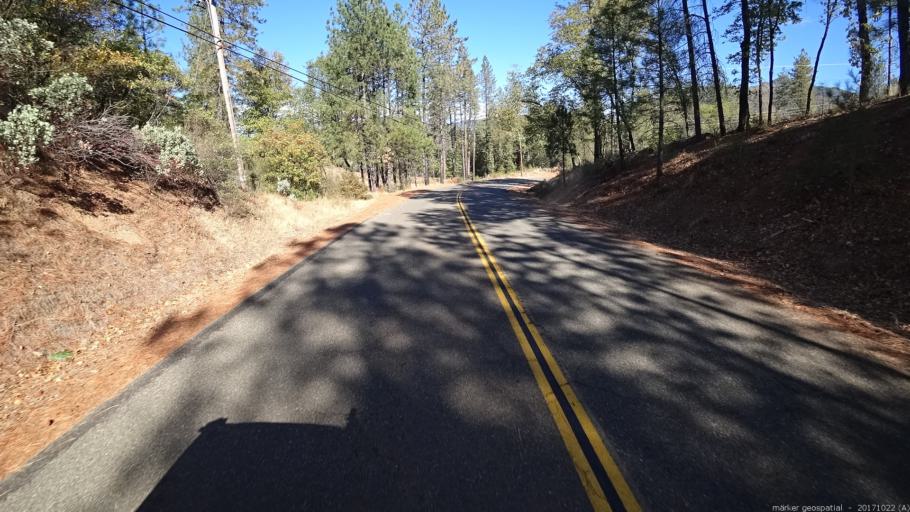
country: US
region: California
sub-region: Shasta County
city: Central Valley (historical)
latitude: 40.8966
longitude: -122.3860
